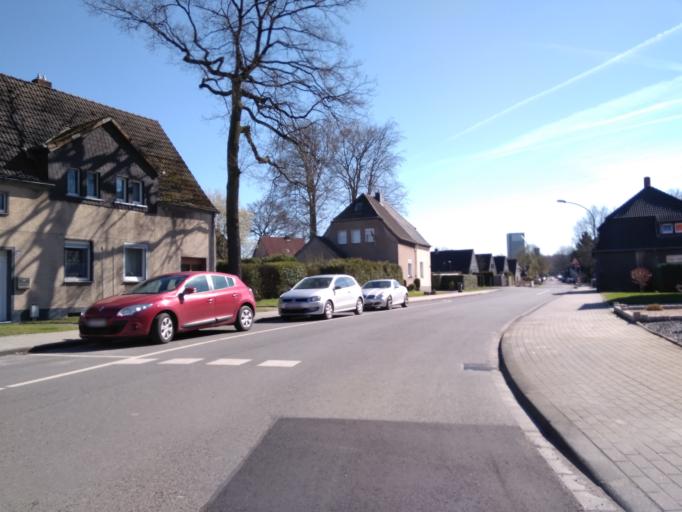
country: DE
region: North Rhine-Westphalia
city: Marl
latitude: 51.6101
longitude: 7.0731
